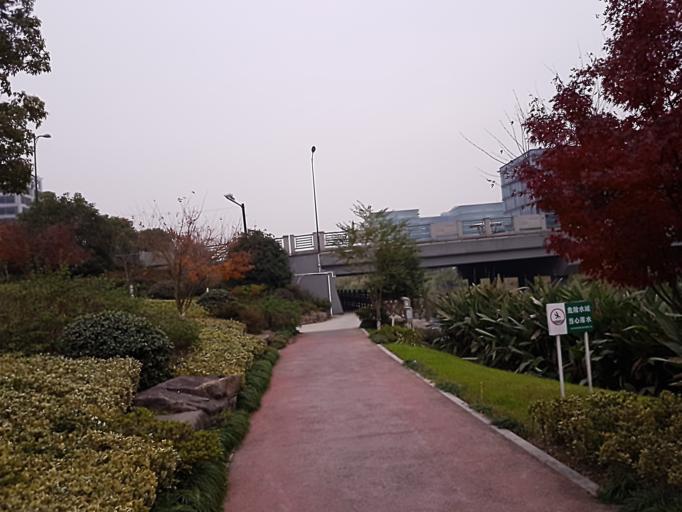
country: CN
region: Zhejiang Sheng
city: Cangqian
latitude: 30.2852
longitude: 120.0095
